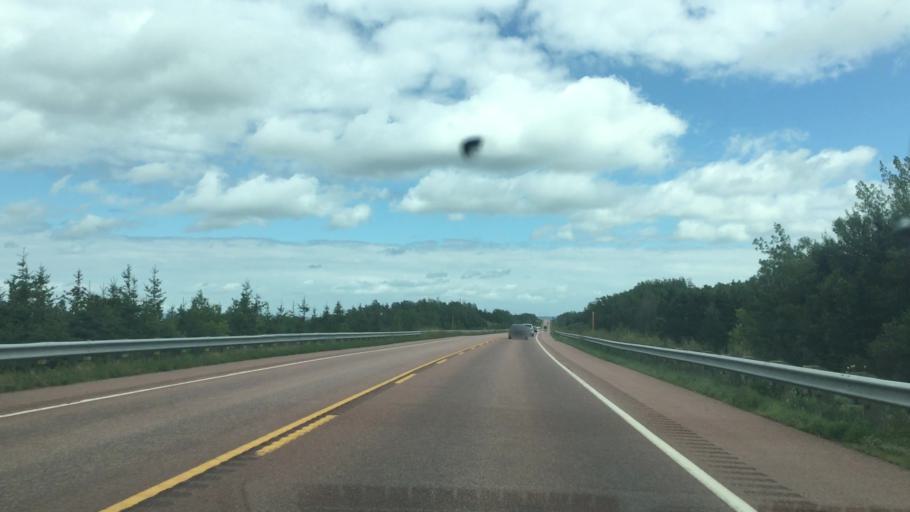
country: CA
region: Nova Scotia
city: Antigonish
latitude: 45.6029
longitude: -61.6949
